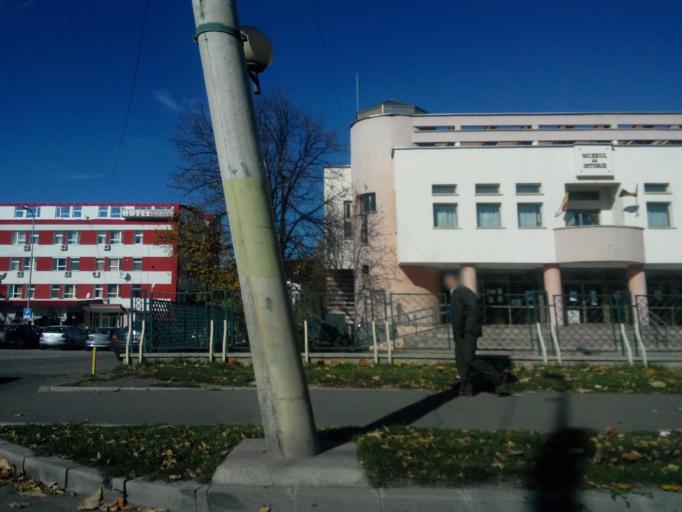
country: RO
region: Bacau
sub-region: Municipiul Onesti
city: Onesti
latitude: 46.2546
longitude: 26.7740
